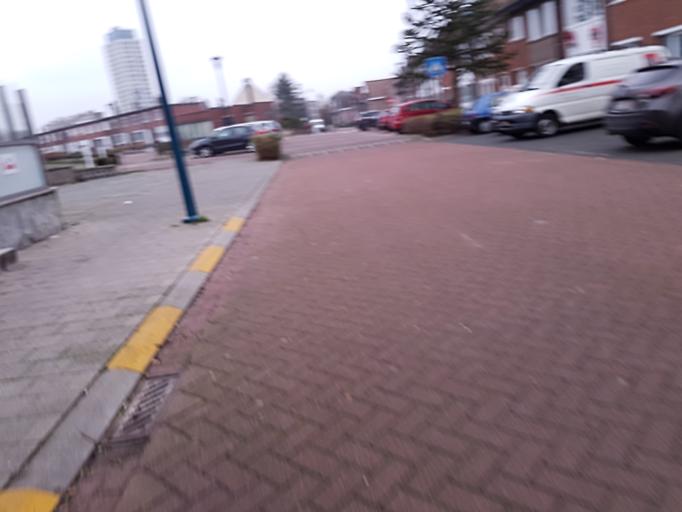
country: BE
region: Flanders
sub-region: Provincie Antwerpen
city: Boom
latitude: 51.0999
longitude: 4.3643
